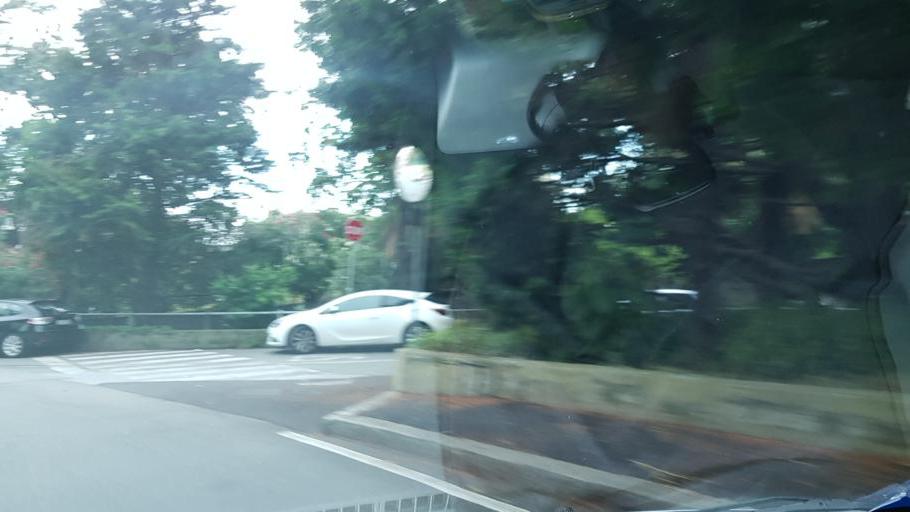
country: IT
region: Liguria
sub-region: Provincia di Genova
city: San Teodoro
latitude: 44.4277
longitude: 8.8337
